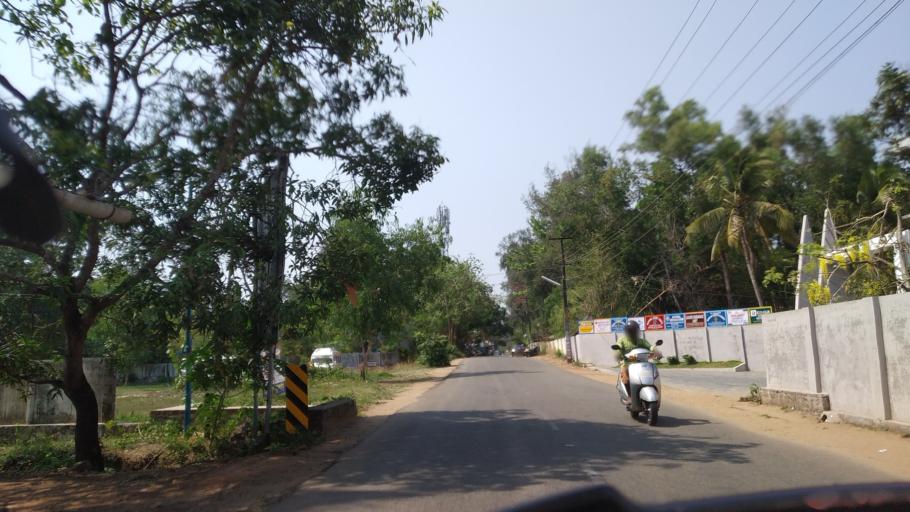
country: IN
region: Kerala
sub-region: Thrissur District
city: Kodungallur
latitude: 10.2656
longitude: 76.1427
